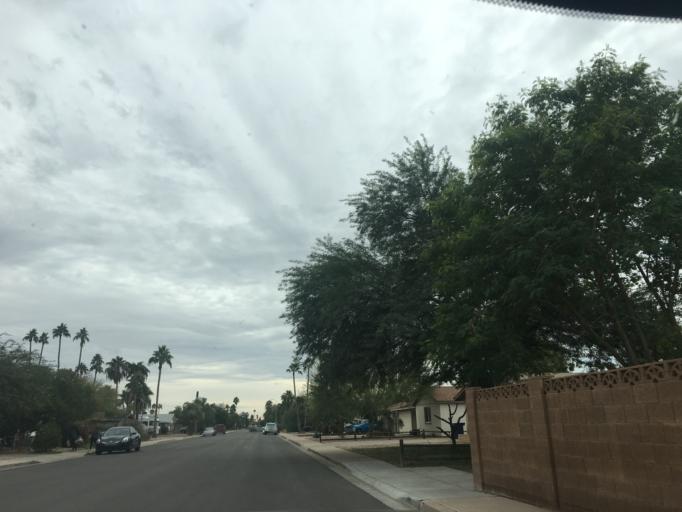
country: US
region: Arizona
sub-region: Maricopa County
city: Tempe
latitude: 33.3814
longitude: -111.9007
